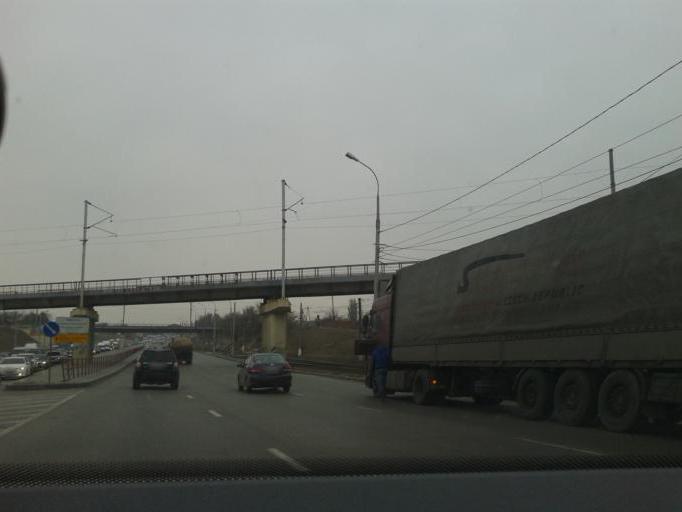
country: RU
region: Volgograd
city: Volgograd
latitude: 48.6865
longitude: 44.4535
